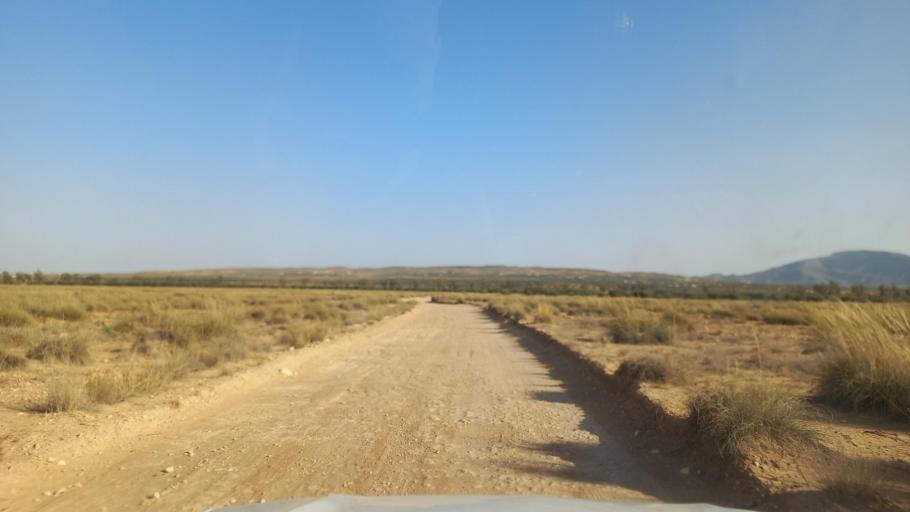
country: TN
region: Al Qasrayn
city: Kasserine
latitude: 35.2310
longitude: 8.9404
